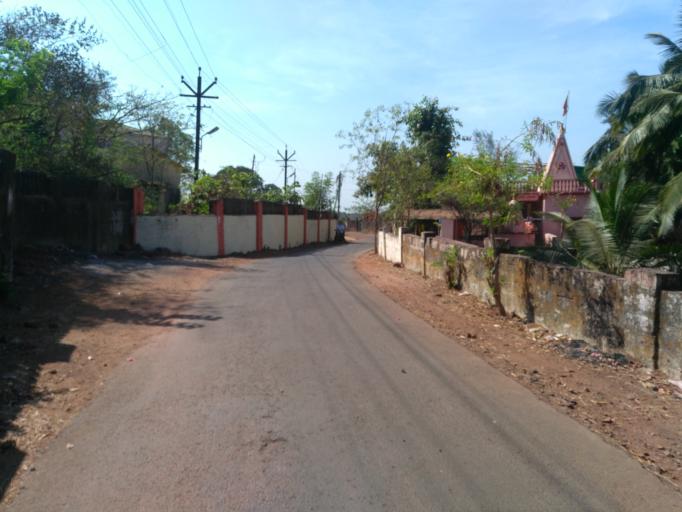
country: IN
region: Maharashtra
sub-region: Ratnagiri
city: Ratnagiri
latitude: 16.9830
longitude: 73.3106
